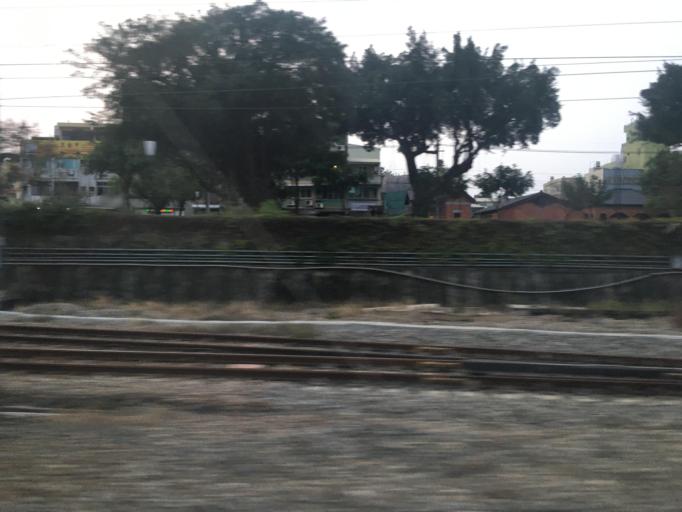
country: TW
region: Taiwan
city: Fengshan
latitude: 22.6573
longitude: 120.4215
